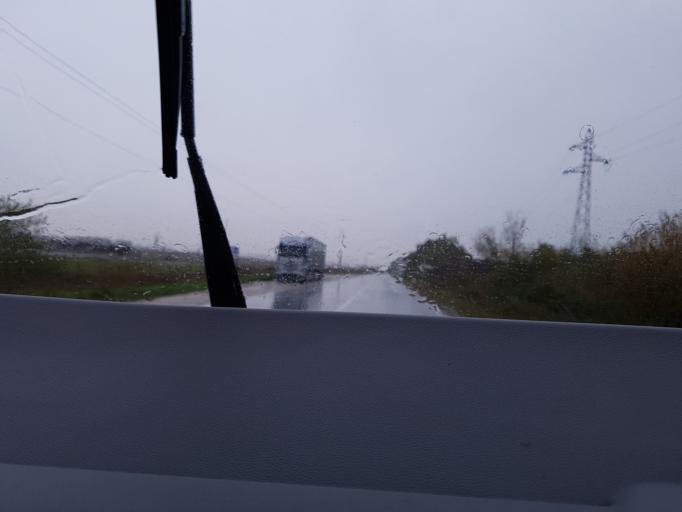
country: FR
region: Aquitaine
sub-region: Departement de la Gironde
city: Saint-Louis-de-Montferrand
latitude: 44.9572
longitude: -0.5181
